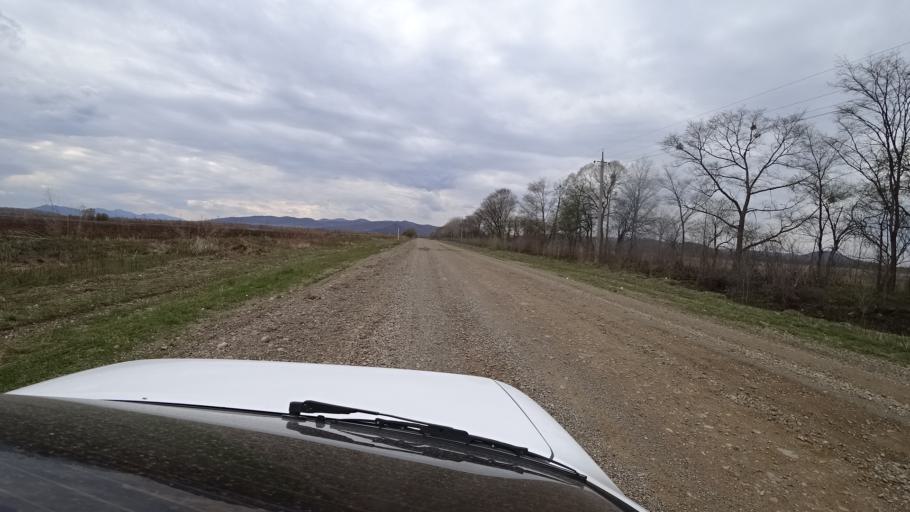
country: RU
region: Primorskiy
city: Novopokrovka
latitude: 45.5766
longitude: 134.3091
